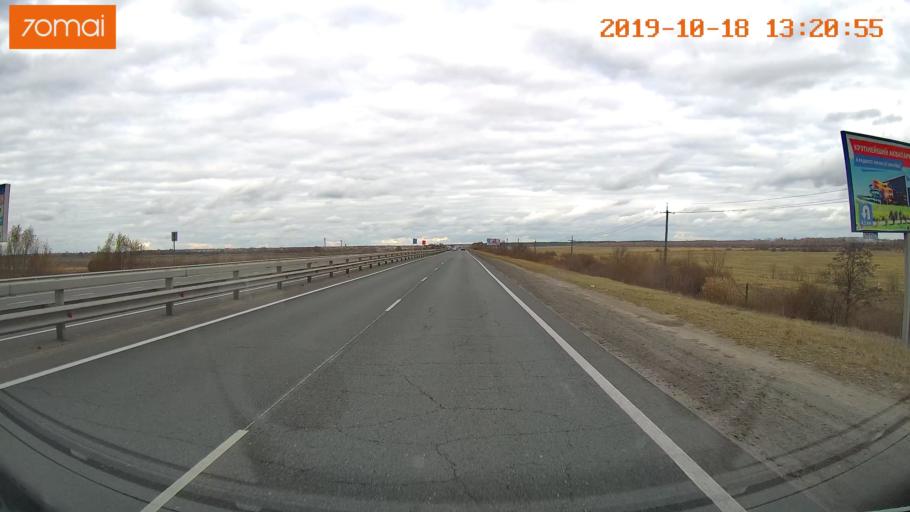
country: RU
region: Rjazan
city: Polyany
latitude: 54.6877
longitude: 39.8355
